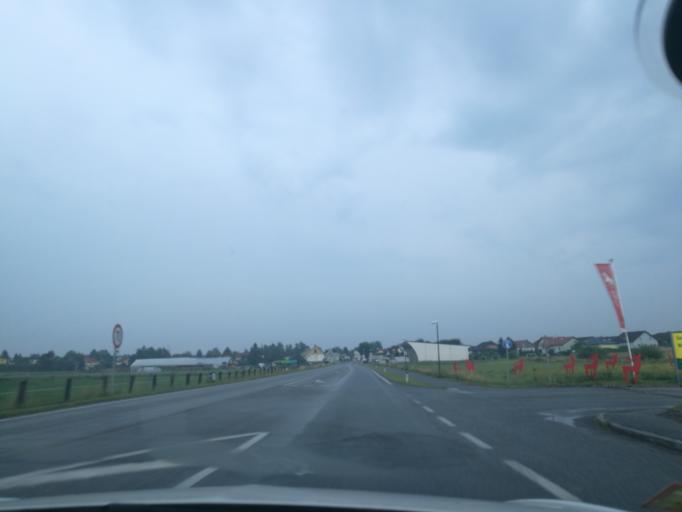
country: AT
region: Lower Austria
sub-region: Politischer Bezirk Zwettl
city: Gopfritz an der Wild
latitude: 48.7282
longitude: 15.3930
